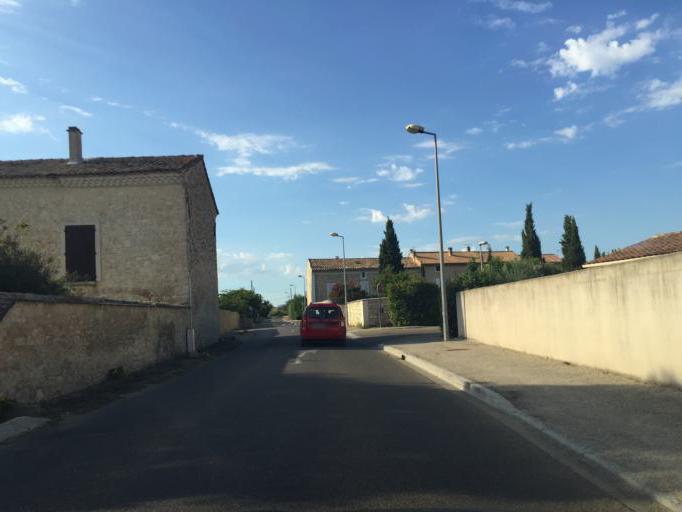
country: FR
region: Provence-Alpes-Cote d'Azur
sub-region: Departement du Vaucluse
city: Pernes-les-Fontaines
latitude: 44.0060
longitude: 5.0561
